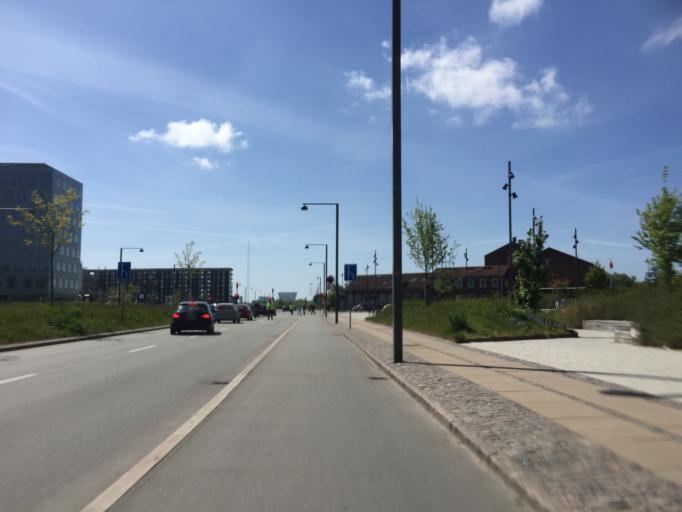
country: DK
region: Capital Region
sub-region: Kobenhavn
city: Christianshavn
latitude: 55.6651
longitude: 12.5853
